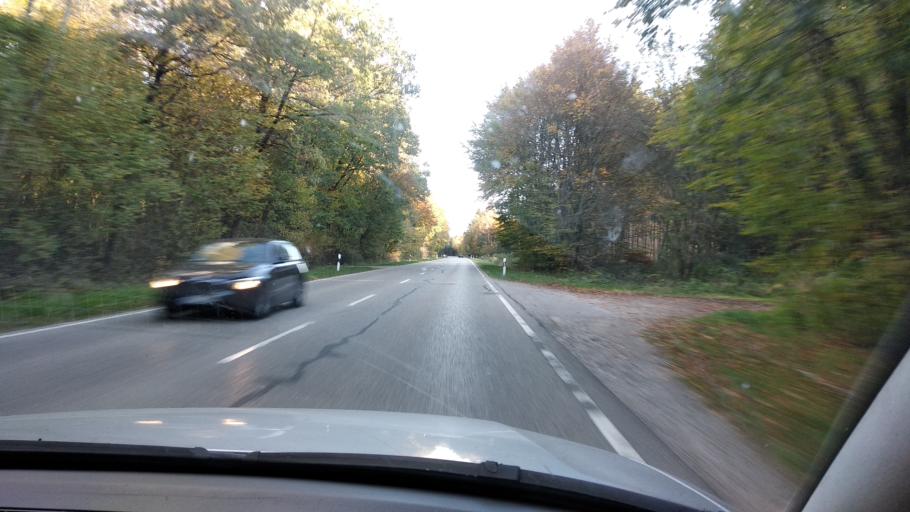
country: DE
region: Bavaria
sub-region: Upper Bavaria
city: Grasbrunn
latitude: 48.0671
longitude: 11.7349
